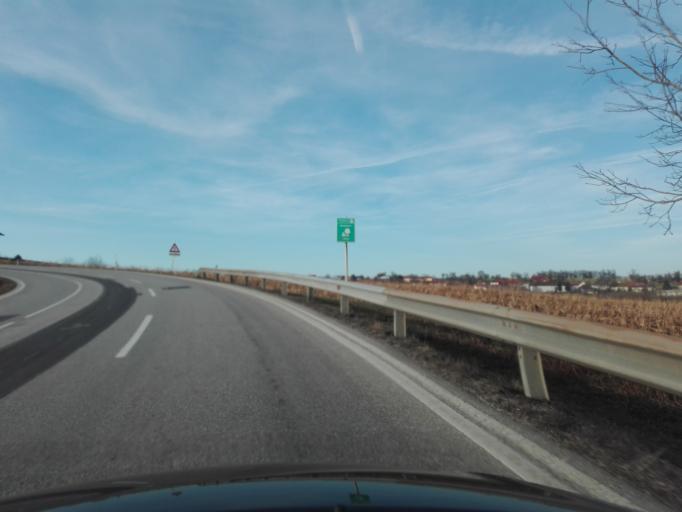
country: AT
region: Lower Austria
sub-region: Politischer Bezirk Amstetten
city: Strengberg
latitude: 48.1441
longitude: 14.6680
